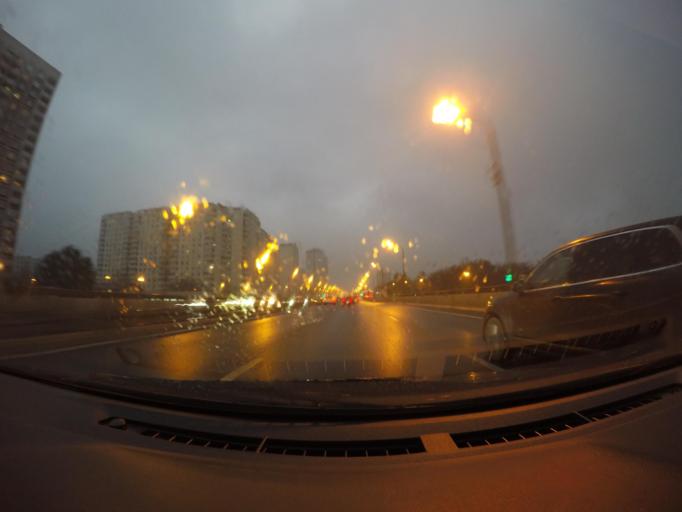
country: RU
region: Moscow
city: Nagornyy
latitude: 55.6415
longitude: 37.6199
